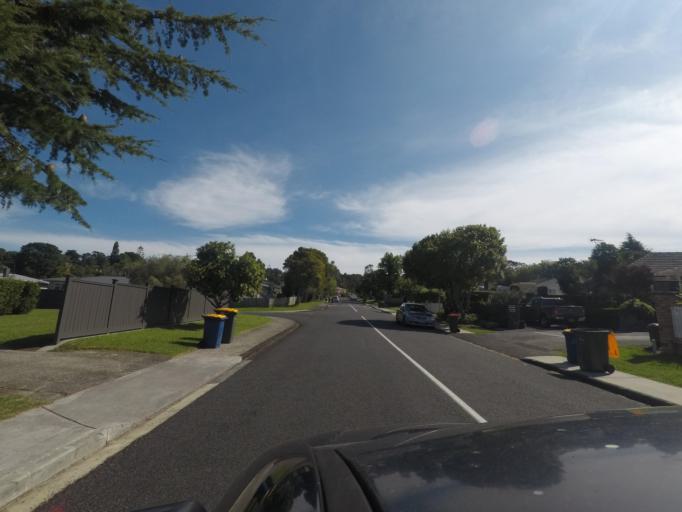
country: NZ
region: Auckland
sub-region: Auckland
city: Titirangi
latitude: -36.9294
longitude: 174.6669
